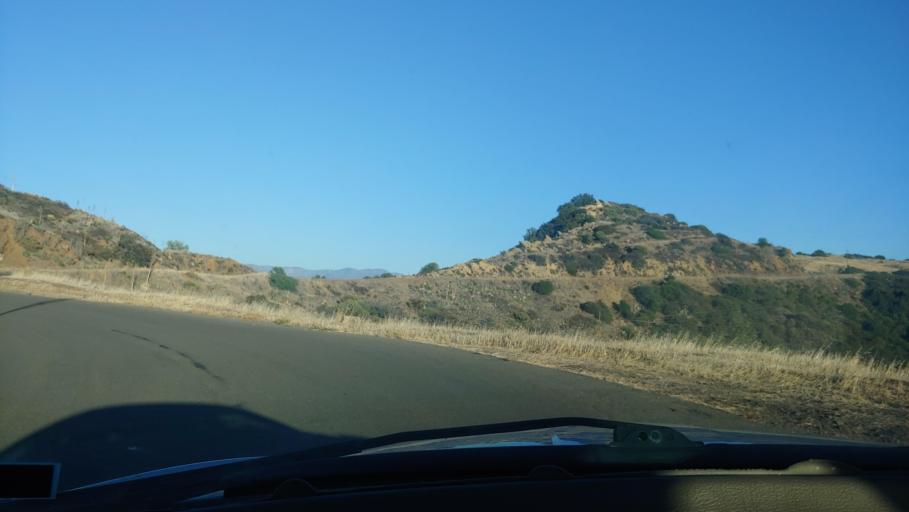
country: US
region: California
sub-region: Santa Barbara County
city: Goleta
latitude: 34.5185
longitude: -119.7857
